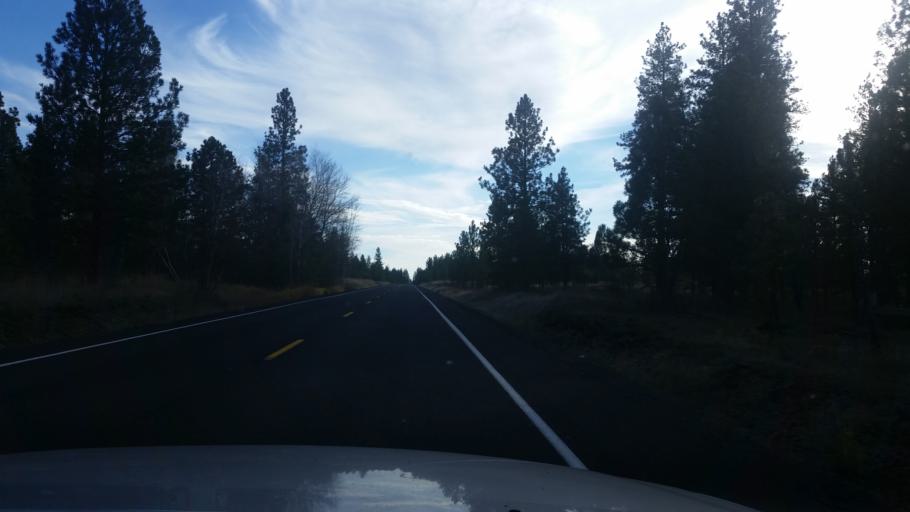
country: US
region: Washington
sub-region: Spokane County
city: Cheney
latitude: 47.4110
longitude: -117.5688
